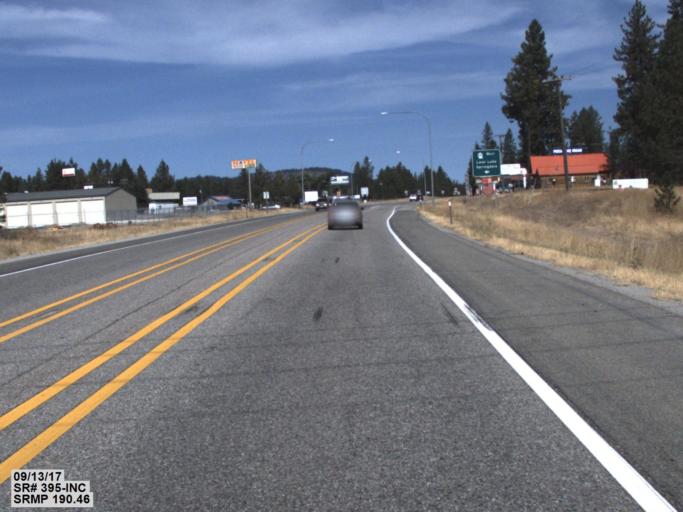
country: US
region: Washington
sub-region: Spokane County
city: Deer Park
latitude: 48.0584
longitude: -117.6195
